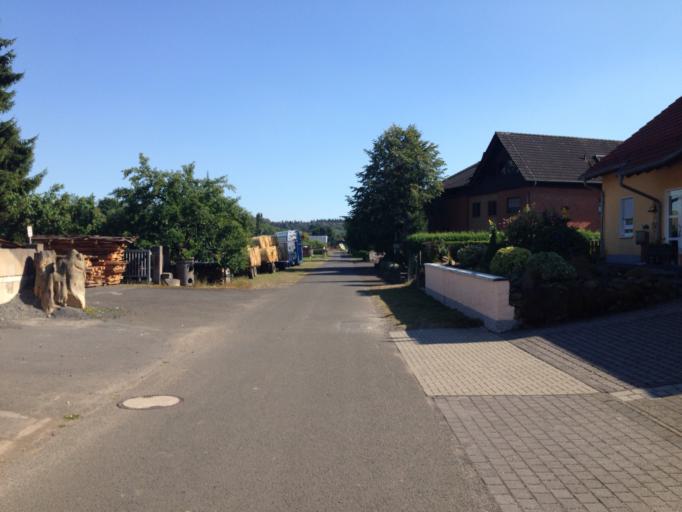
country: DE
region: Hesse
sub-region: Regierungsbezirk Giessen
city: Rabenau
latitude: 50.6495
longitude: 8.8949
